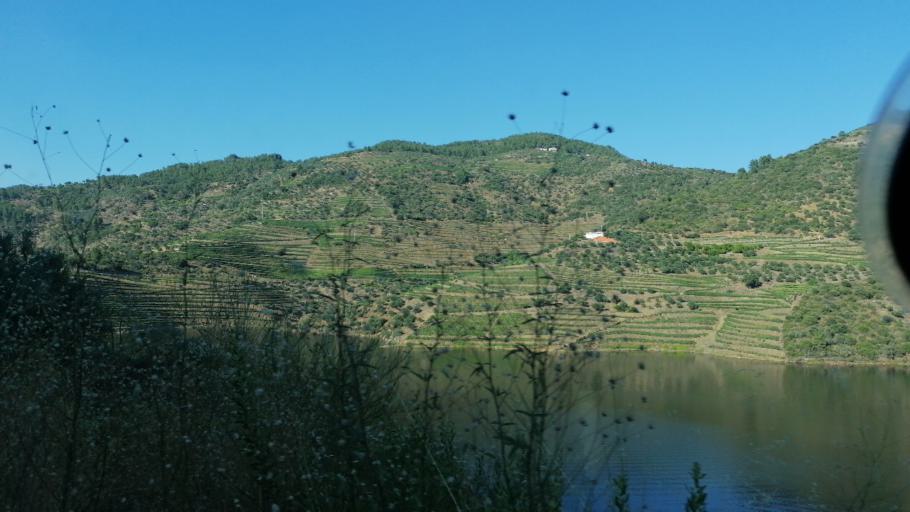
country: PT
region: Viseu
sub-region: Sao Joao da Pesqueira
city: Sao Joao da Pesqueira
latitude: 41.2282
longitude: -7.4238
